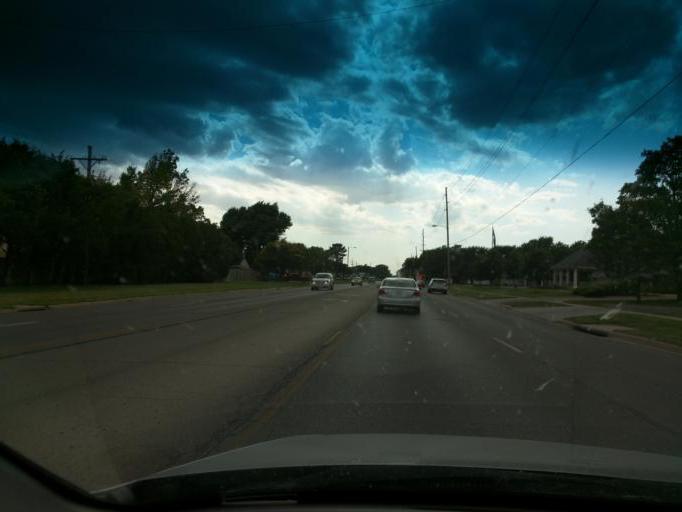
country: US
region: Kansas
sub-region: Reno County
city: Hutchinson
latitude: 38.0866
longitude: -97.9248
